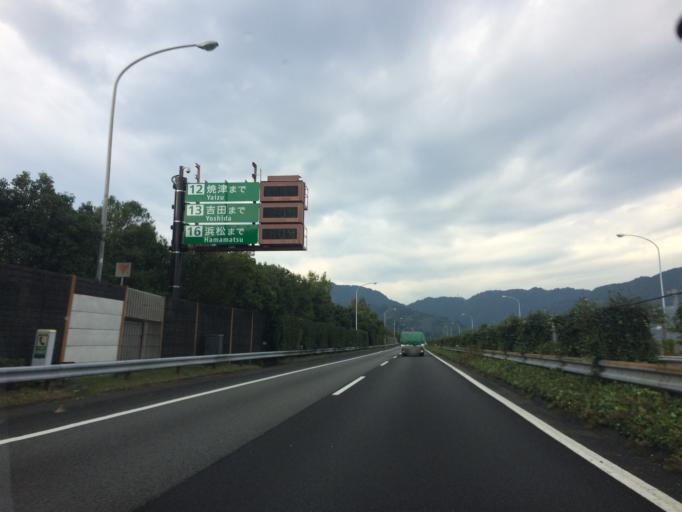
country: JP
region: Shizuoka
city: Shizuoka-shi
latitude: 34.9348
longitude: 138.3737
